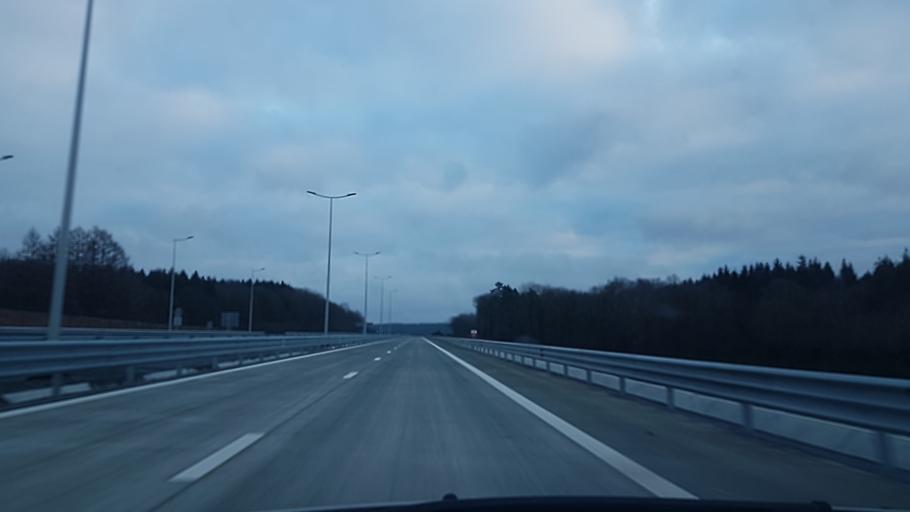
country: BE
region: Wallonia
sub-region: Province de Namur
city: Couvin
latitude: 50.0212
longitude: 4.5252
